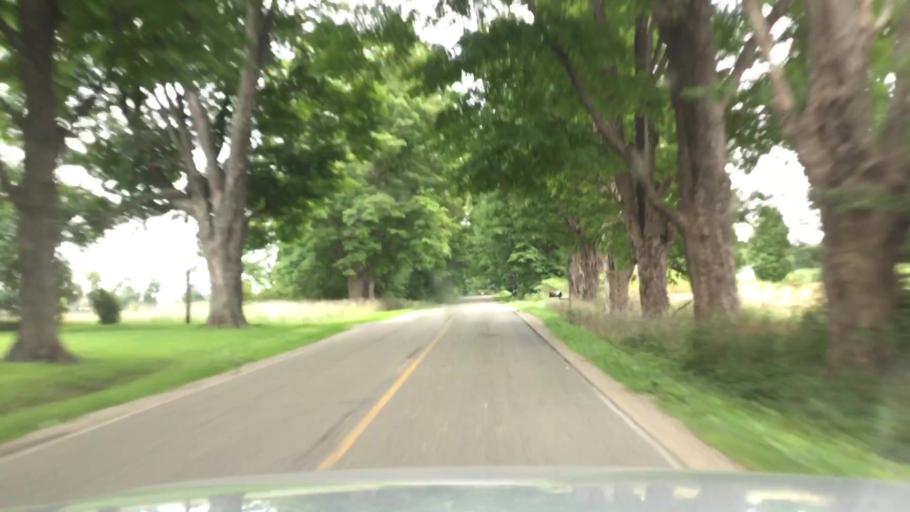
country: US
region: Michigan
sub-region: Shiawassee County
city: Durand
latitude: 42.8298
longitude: -84.0196
